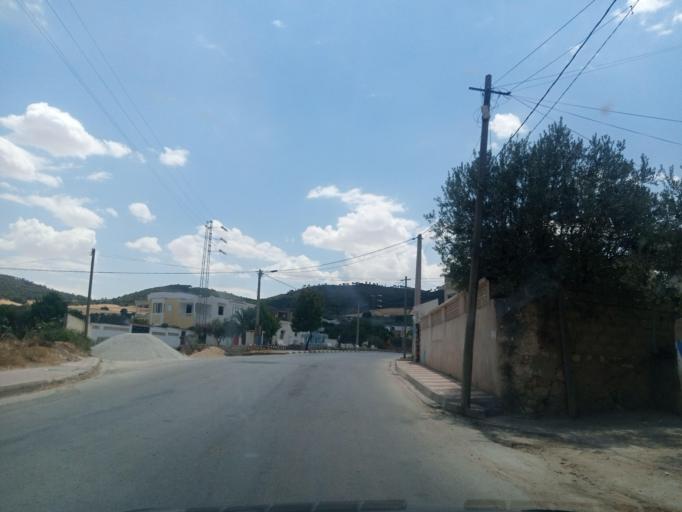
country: TN
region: Kef
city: Nibbar
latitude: 36.2973
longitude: 8.7699
